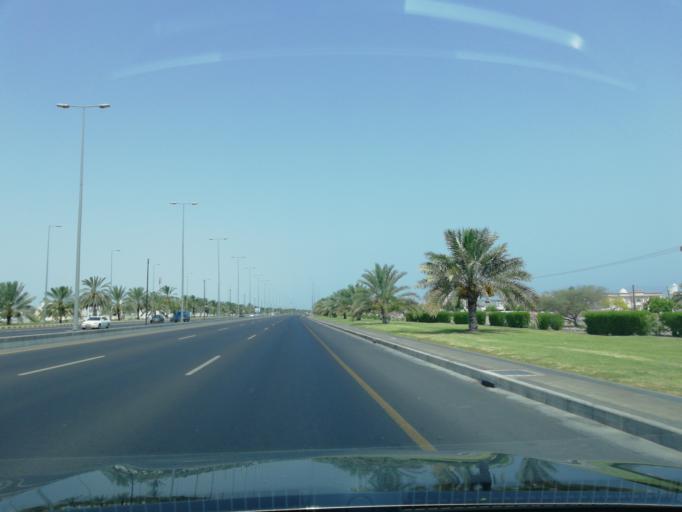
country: OM
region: Muhafazat Masqat
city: As Sib al Jadidah
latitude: 23.6809
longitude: 58.1118
